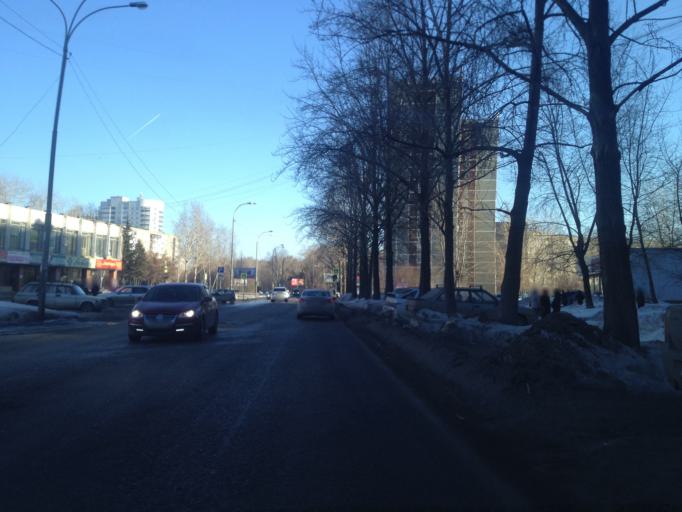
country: RU
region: Sverdlovsk
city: Yekaterinburg
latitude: 56.8680
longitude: 60.5565
